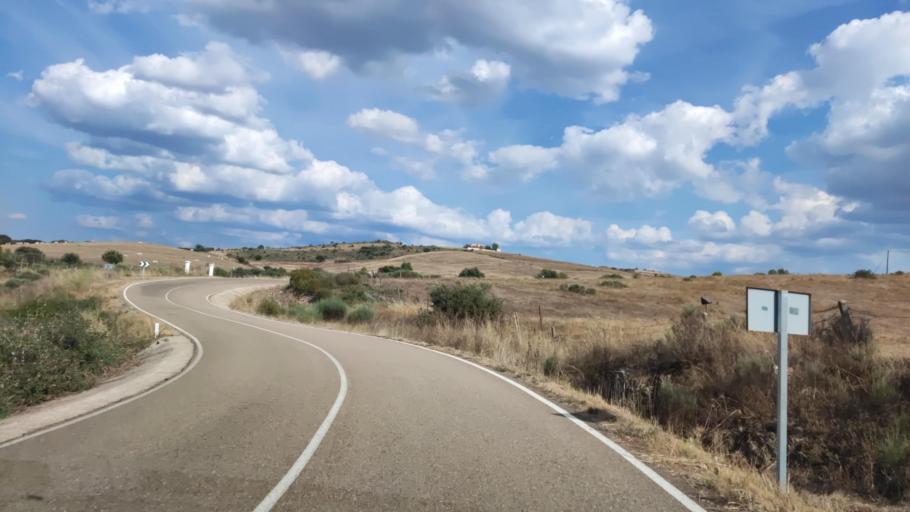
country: ES
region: Castille and Leon
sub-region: Provincia de Salamanca
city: Pastores
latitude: 40.5205
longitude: -6.5164
